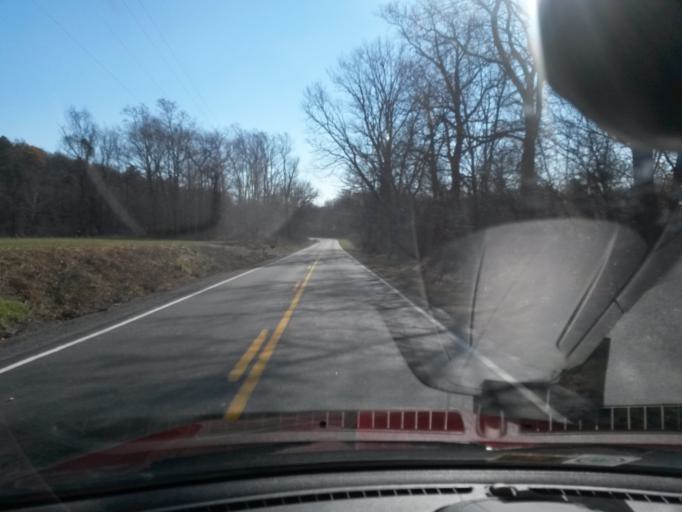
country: US
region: Virginia
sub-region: City of Bedford
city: Bedford
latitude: 37.4237
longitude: -79.5727
